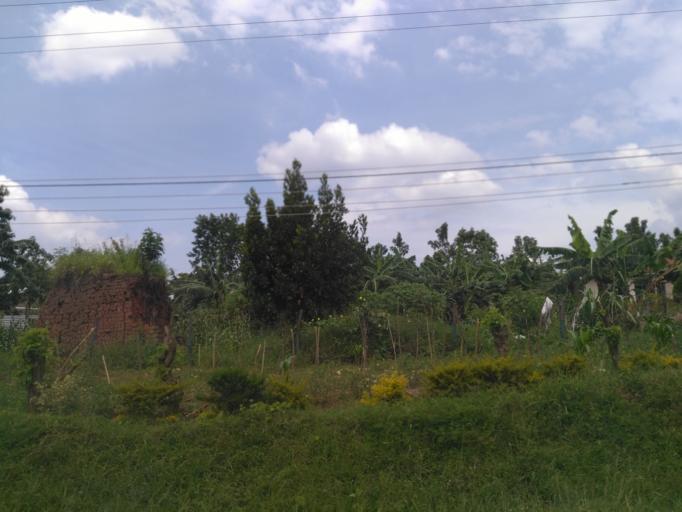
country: UG
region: Central Region
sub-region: Wakiso District
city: Bweyogerere
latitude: 0.4595
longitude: 32.6182
